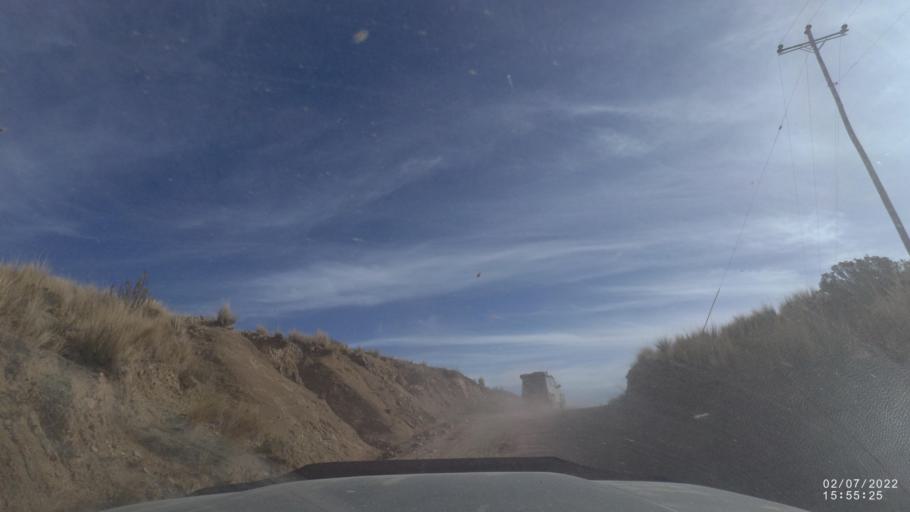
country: BO
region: Cochabamba
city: Irpa Irpa
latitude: -17.9094
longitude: -66.4209
